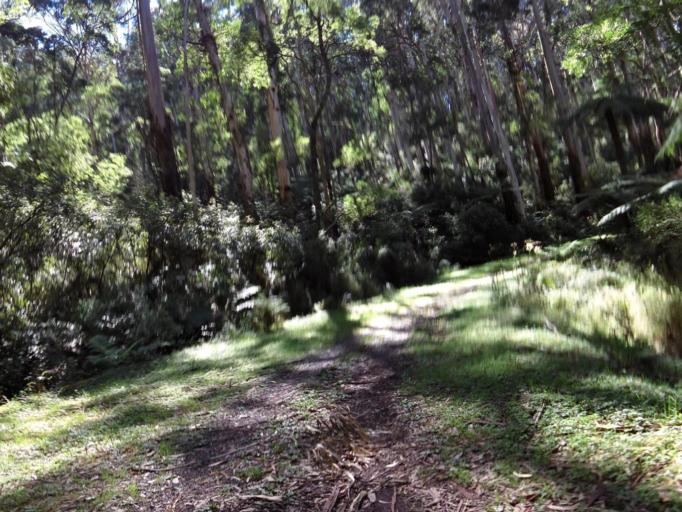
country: AU
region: Victoria
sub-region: Yarra Ranges
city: Yarra Junction
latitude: -37.7446
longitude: 145.6131
